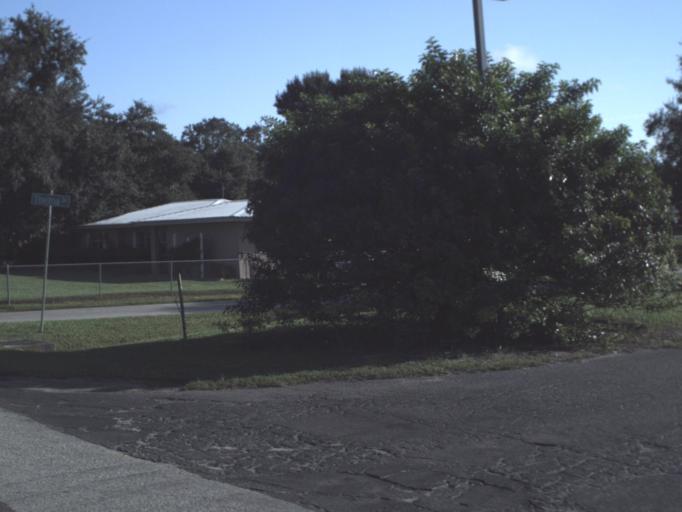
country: US
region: Florida
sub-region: Polk County
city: Combee Settlement
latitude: 28.0630
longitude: -81.9080
